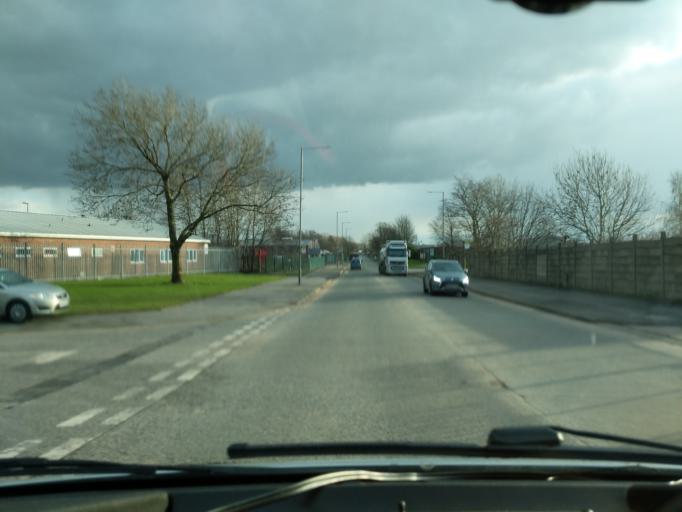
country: GB
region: England
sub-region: St. Helens
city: St Helens
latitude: 53.4501
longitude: -2.7220
